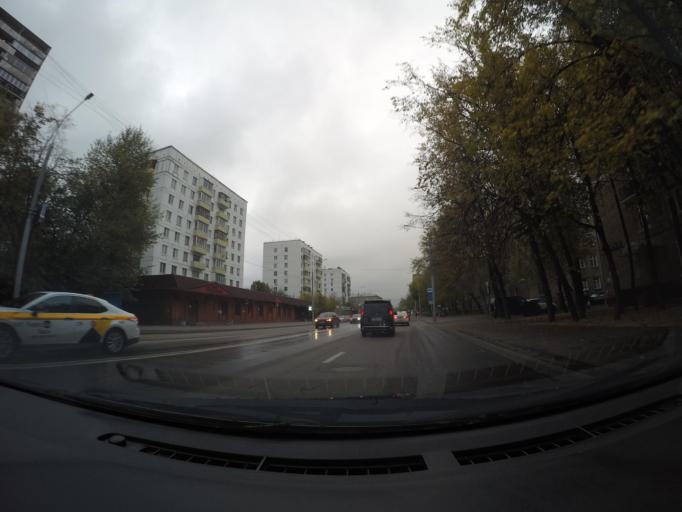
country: RU
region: Moskovskaya
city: Novogireyevo
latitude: 55.7577
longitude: 37.7960
